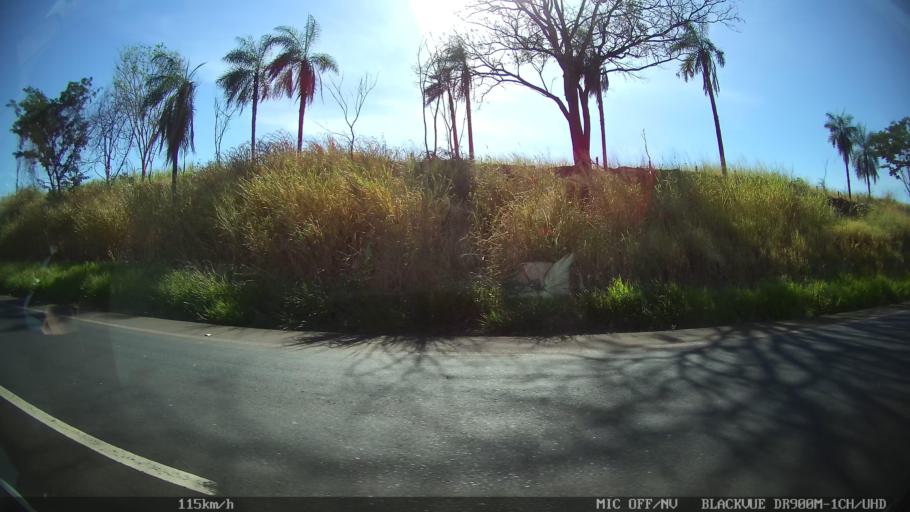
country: BR
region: Sao Paulo
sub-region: Barretos
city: Barretos
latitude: -20.5985
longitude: -48.7226
